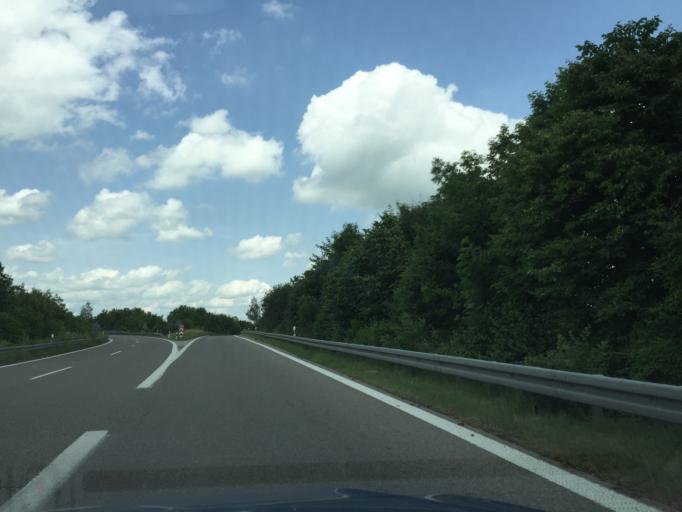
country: DE
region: Bavaria
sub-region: Swabia
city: Nersingen
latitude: 48.4607
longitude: 10.1177
